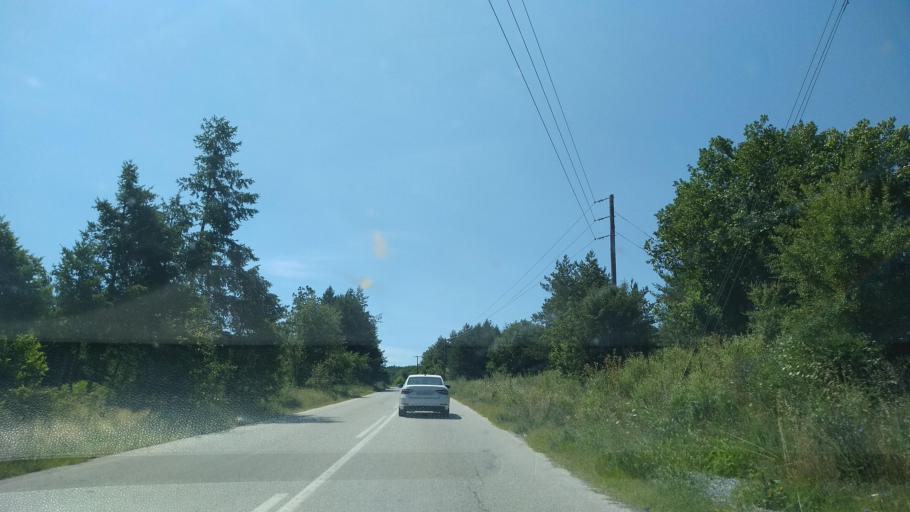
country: GR
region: Central Macedonia
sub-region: Nomos Chalkidikis
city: Palaiochori
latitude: 40.4653
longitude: 23.6513
